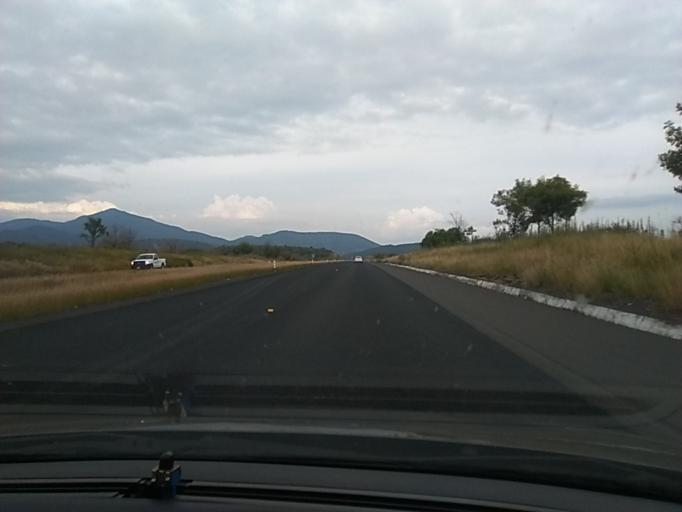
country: MX
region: Mexico
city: Huaniqueo de Morales
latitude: 19.8846
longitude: -101.4869
